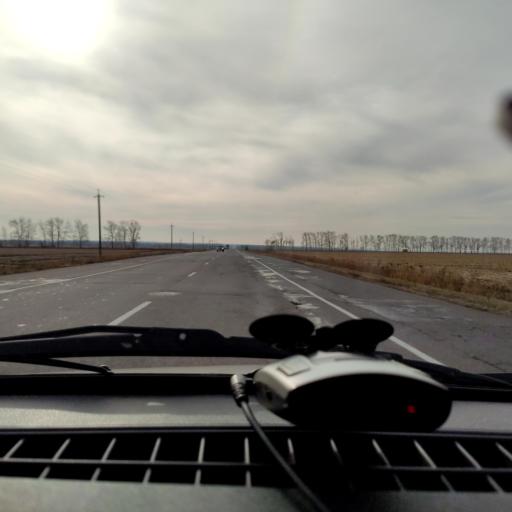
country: RU
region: Voronezj
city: Strelitsa
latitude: 51.5365
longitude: 38.9701
